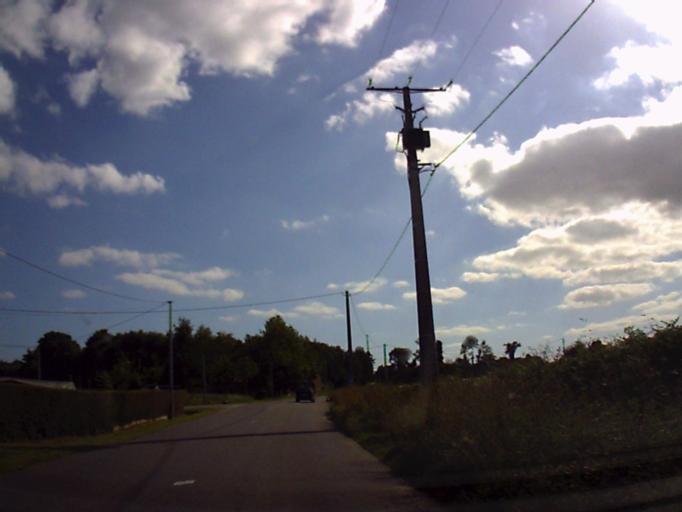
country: FR
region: Brittany
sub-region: Departement d'Ille-et-Vilaine
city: Iffendic
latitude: 48.1662
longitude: -2.0035
